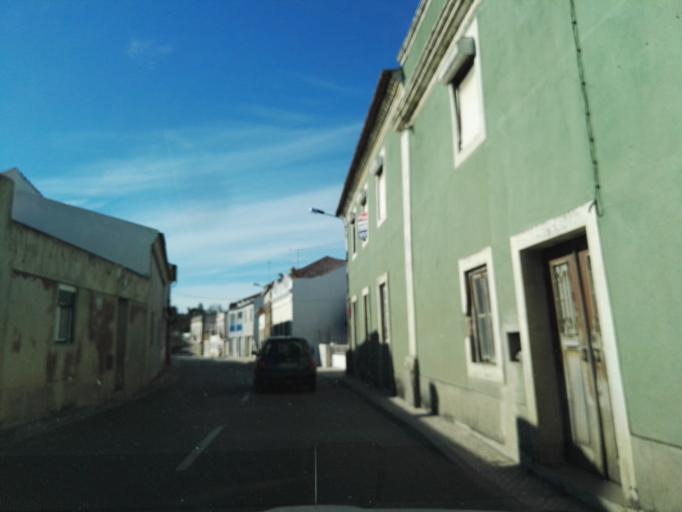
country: PT
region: Santarem
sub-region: Macao
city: Macao
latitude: 39.4659
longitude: -8.0462
